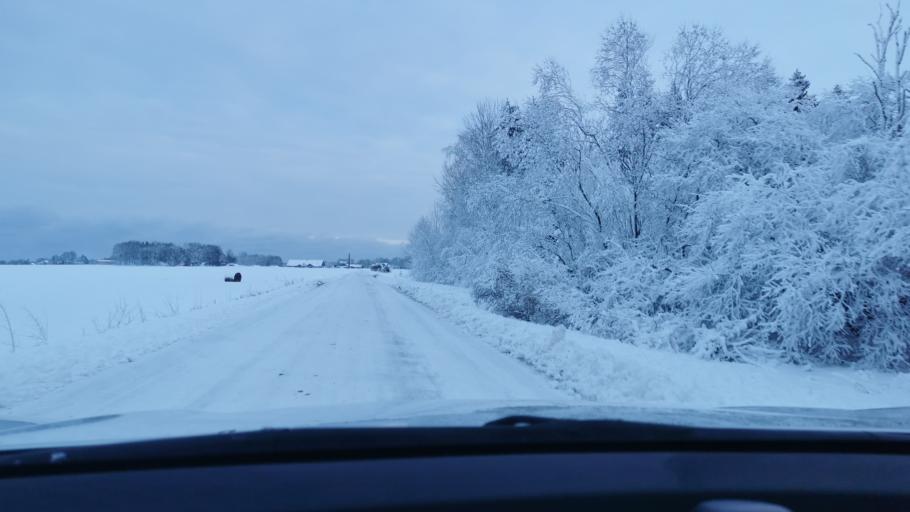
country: EE
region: Laeaene-Virumaa
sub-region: Someru vald
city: Someru
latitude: 59.4899
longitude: 26.3912
